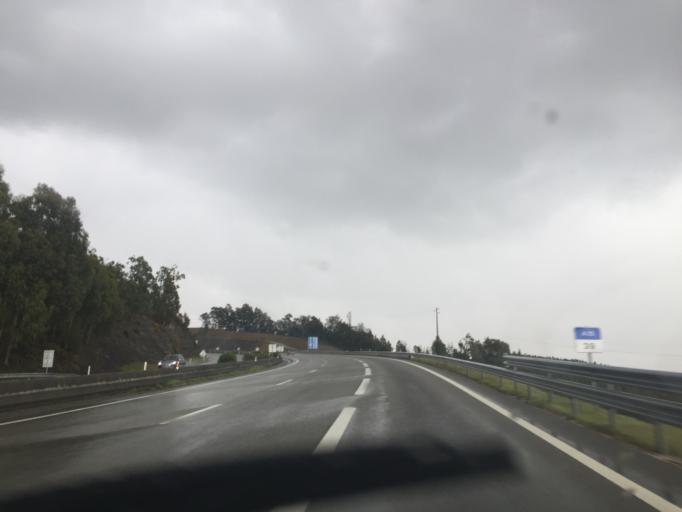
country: PT
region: Aveiro
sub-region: Agueda
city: Valongo
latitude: 40.6512
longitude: -8.3755
